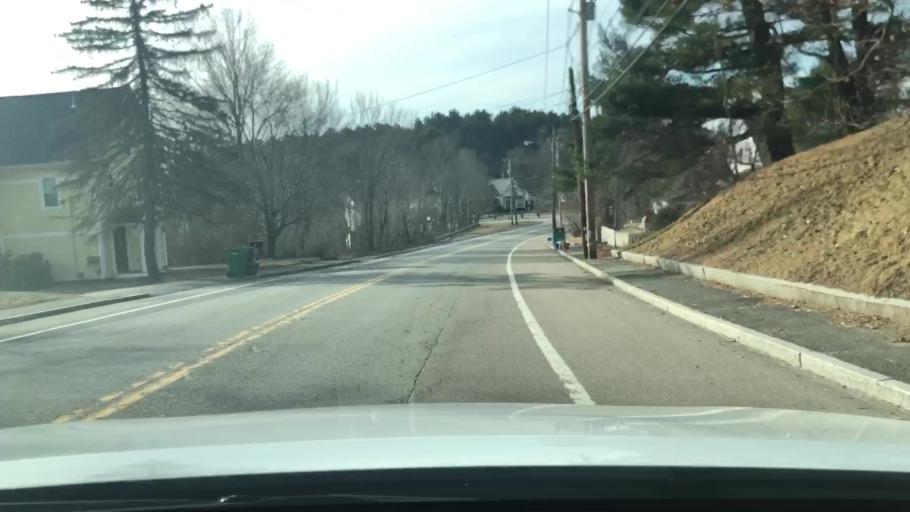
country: US
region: Massachusetts
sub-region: Worcester County
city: Upton
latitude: 42.1689
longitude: -71.6131
